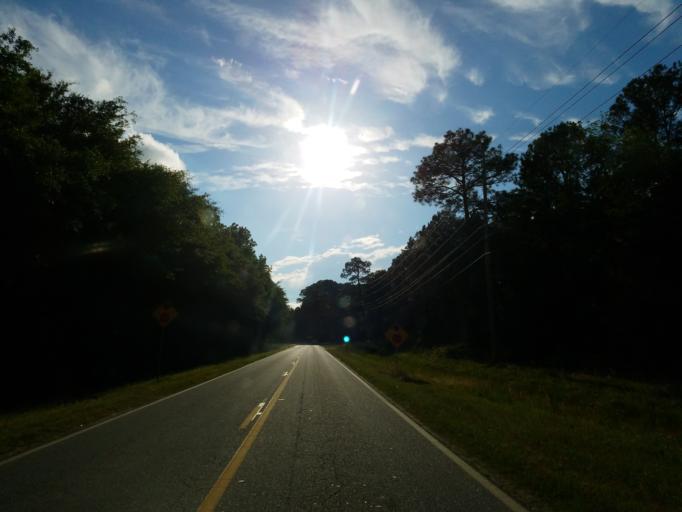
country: US
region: Georgia
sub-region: Crisp County
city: Cordele
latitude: 32.0044
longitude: -83.7918
